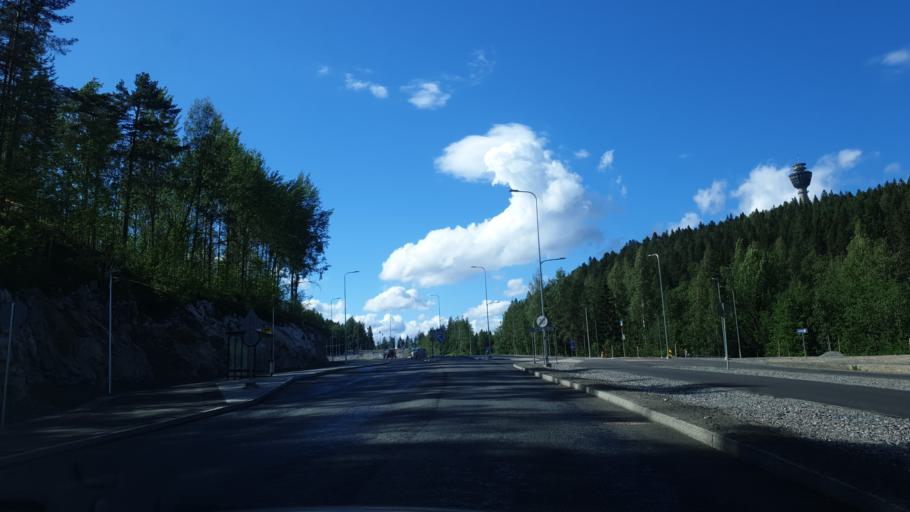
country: FI
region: Northern Savo
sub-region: Kuopio
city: Kuopio
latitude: 62.9031
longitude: 27.6597
